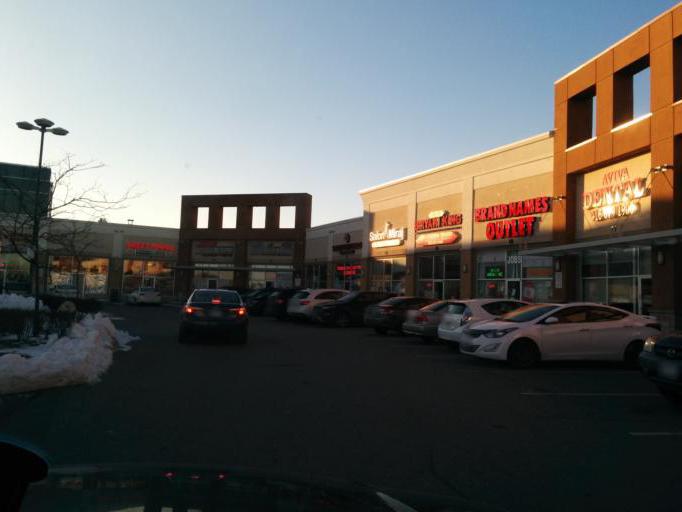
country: CA
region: Ontario
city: Etobicoke
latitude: 43.7209
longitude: -79.6138
